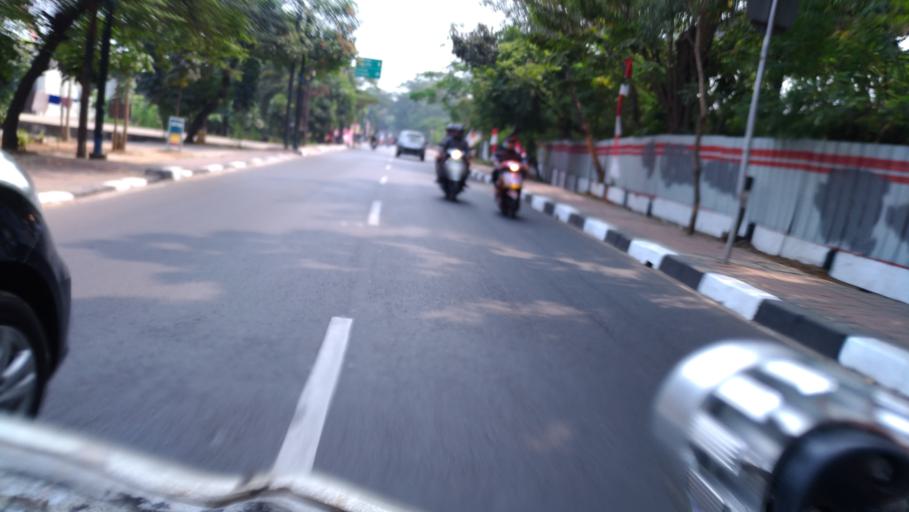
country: ID
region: West Java
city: Cileungsir
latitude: -6.3332
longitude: 106.8870
